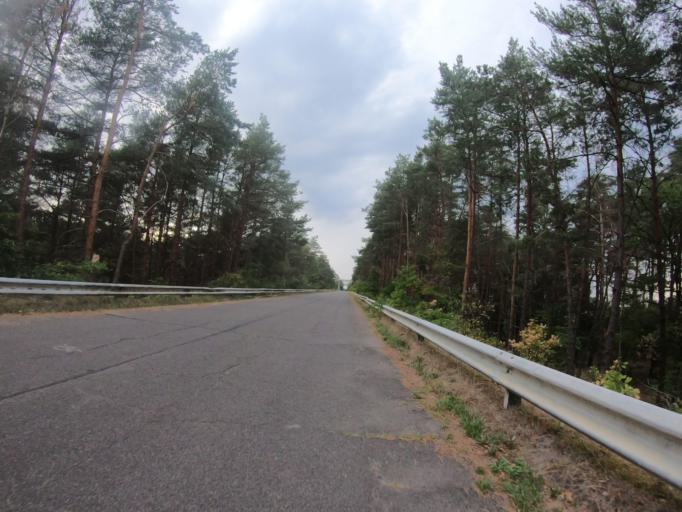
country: DE
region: Lower Saxony
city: Sassenburg
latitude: 52.5564
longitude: 10.6659
